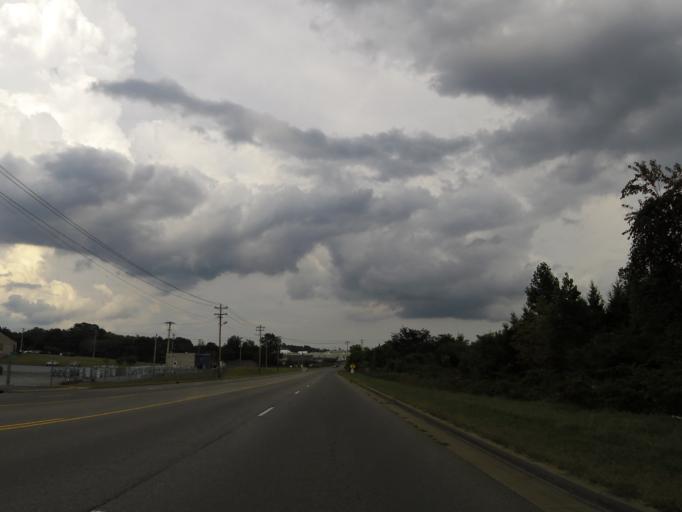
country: US
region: Tennessee
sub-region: Dickson County
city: Dickson
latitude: 36.0644
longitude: -87.3895
